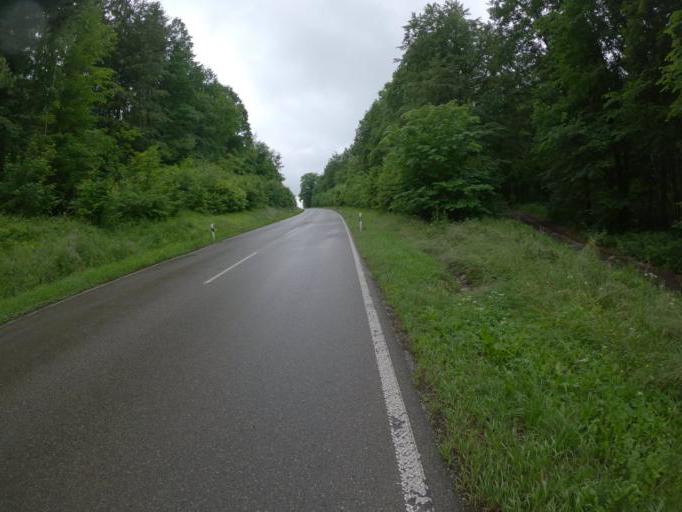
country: DE
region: Baden-Wuerttemberg
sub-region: Regierungsbezirk Stuttgart
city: Adelberg
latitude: 48.7522
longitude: 9.6132
